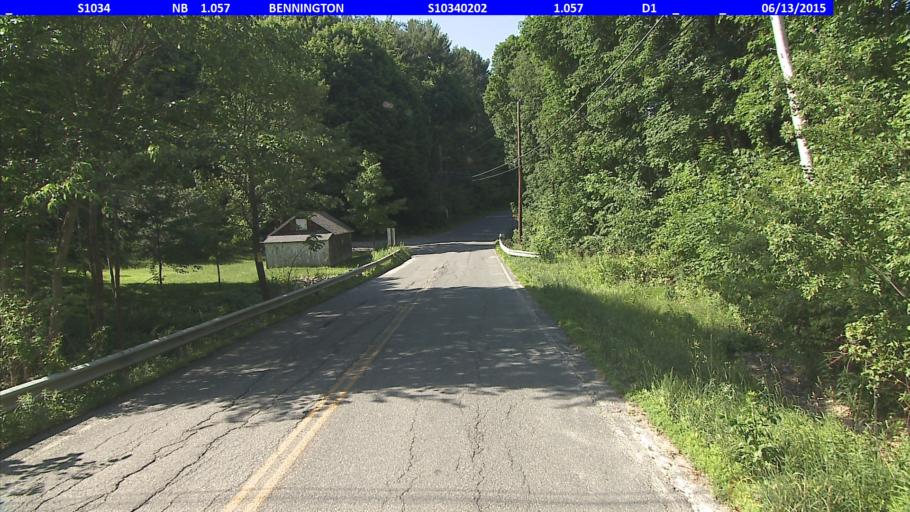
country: US
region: Vermont
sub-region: Bennington County
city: Bennington
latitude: 42.8665
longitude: -73.2093
